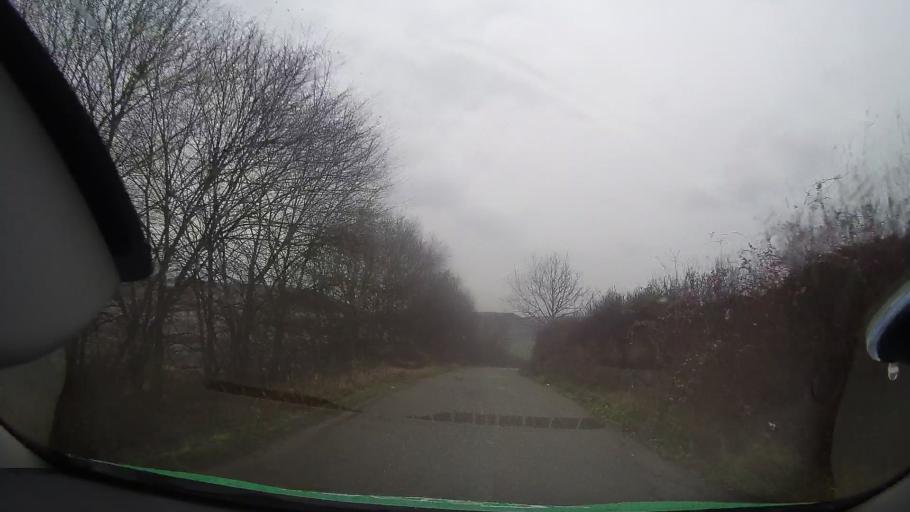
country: RO
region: Bihor
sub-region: Comuna Uileacu de Beius
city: Uileacu de Beius
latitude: 46.6889
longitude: 22.2198
